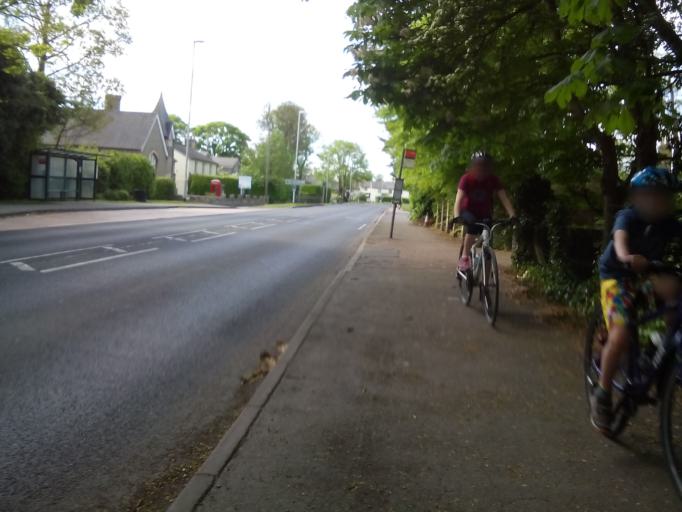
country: GB
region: England
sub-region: Cambridgeshire
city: Harston
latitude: 52.1381
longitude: 0.0812
